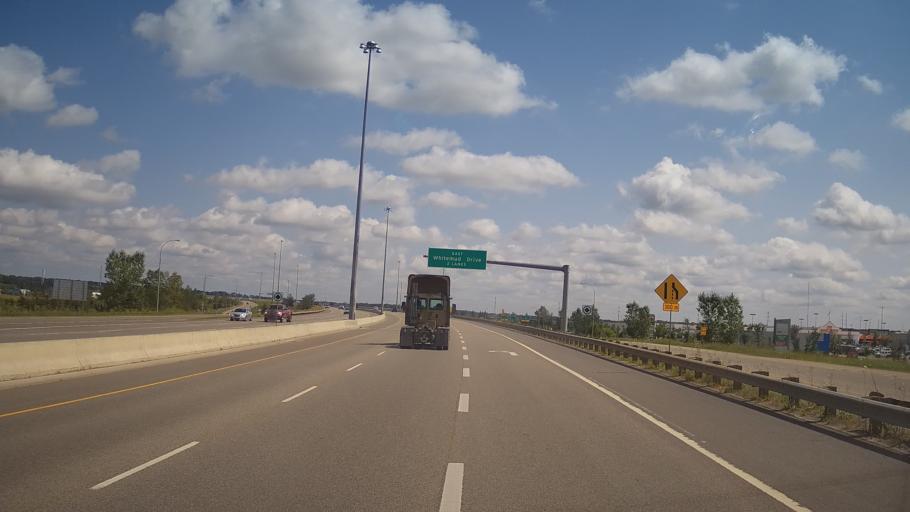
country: CA
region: Alberta
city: Sherwood Park
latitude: 53.4825
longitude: -113.3751
